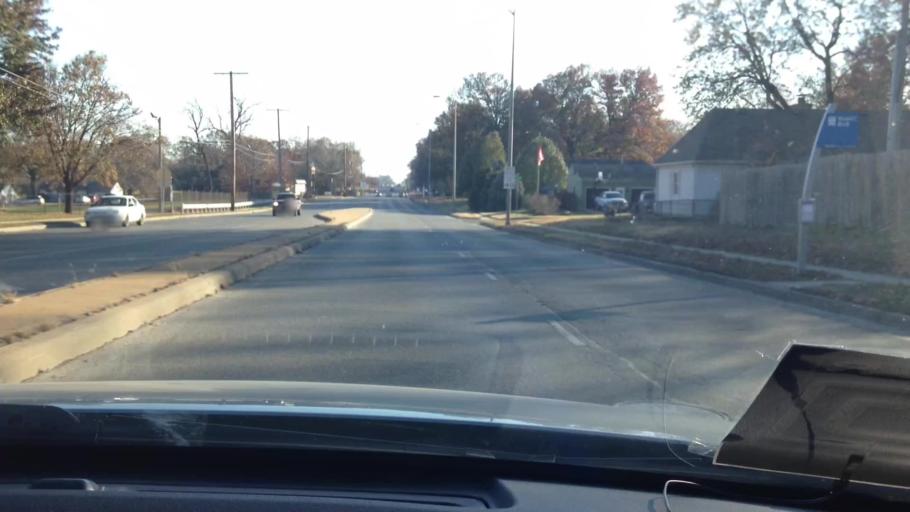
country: US
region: Kansas
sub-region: Johnson County
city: Overland Park
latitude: 39.0002
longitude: -94.6677
